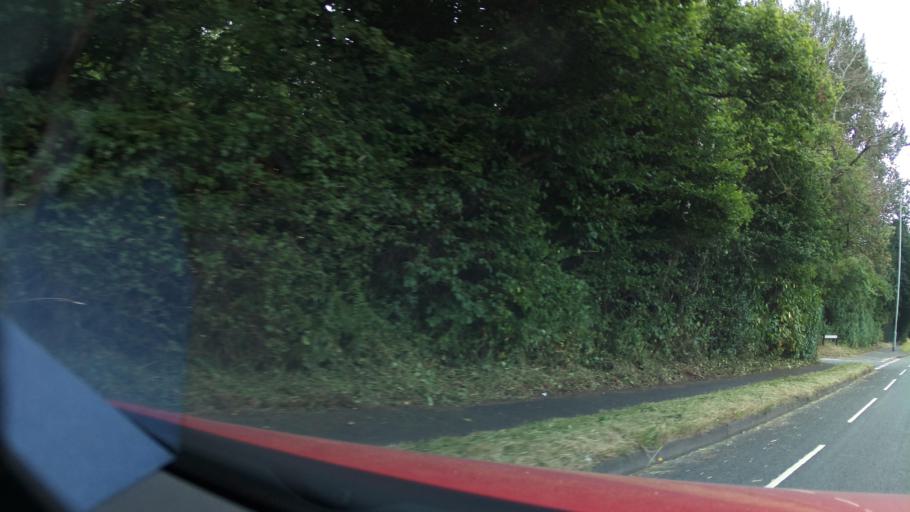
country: GB
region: England
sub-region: Worcestershire
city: Kidderminster
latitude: 52.3765
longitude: -2.2405
